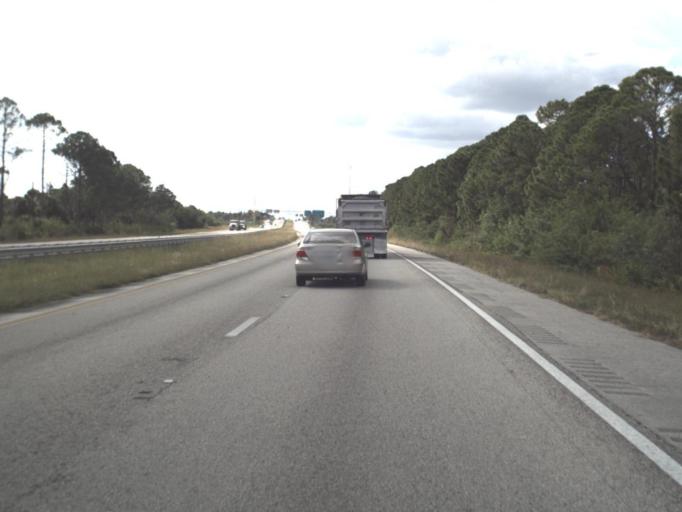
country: US
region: Florida
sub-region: Brevard County
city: Sharpes
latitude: 28.4120
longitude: -80.8097
